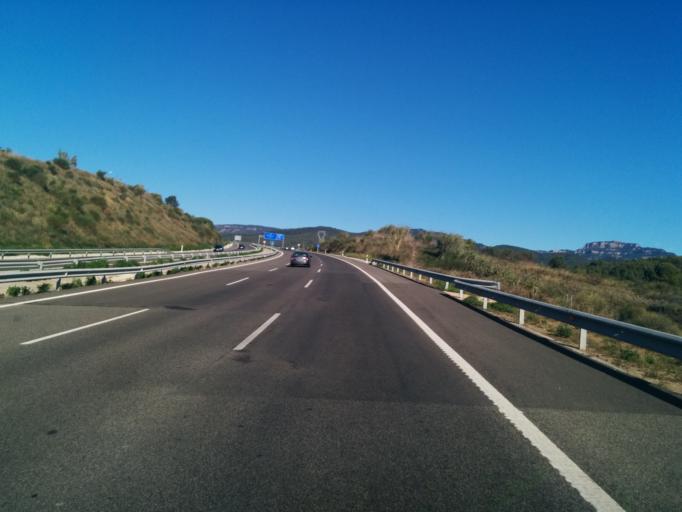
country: ES
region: Catalonia
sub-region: Provincia de Barcelona
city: Terrassa
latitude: 41.5720
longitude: 1.9903
